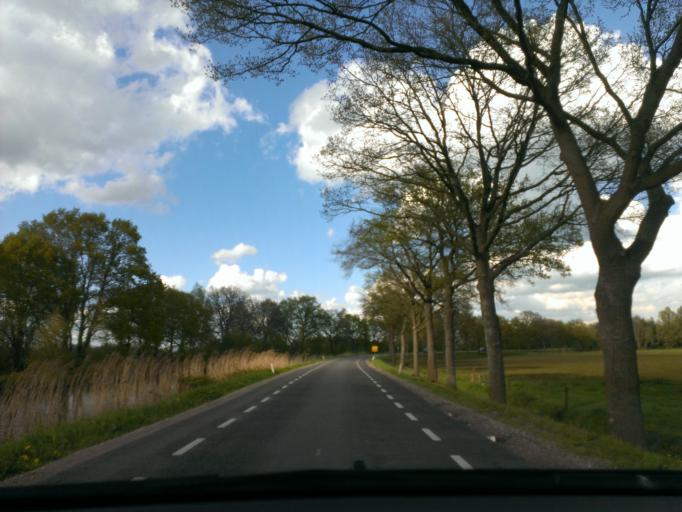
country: NL
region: Gelderland
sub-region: Gemeente Epe
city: Oene
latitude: 52.3567
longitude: 6.0252
